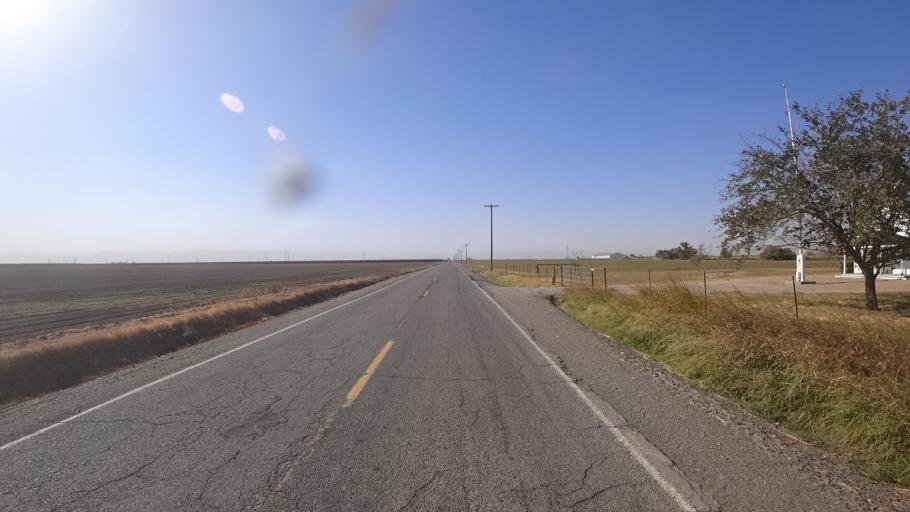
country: US
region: California
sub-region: Yolo County
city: Cottonwood
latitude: 38.7153
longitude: -121.9291
